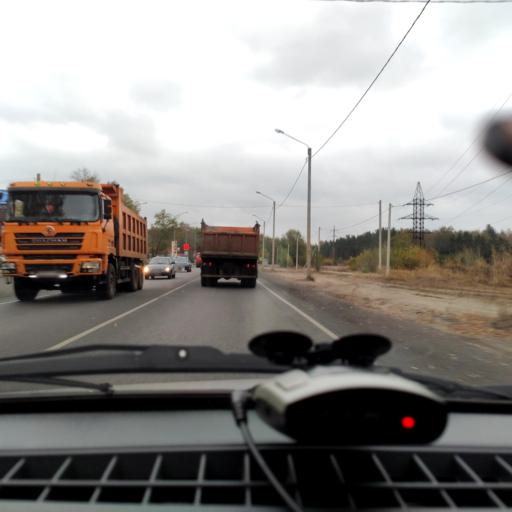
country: RU
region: Voronezj
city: Pridonskoy
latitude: 51.6968
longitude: 39.0856
